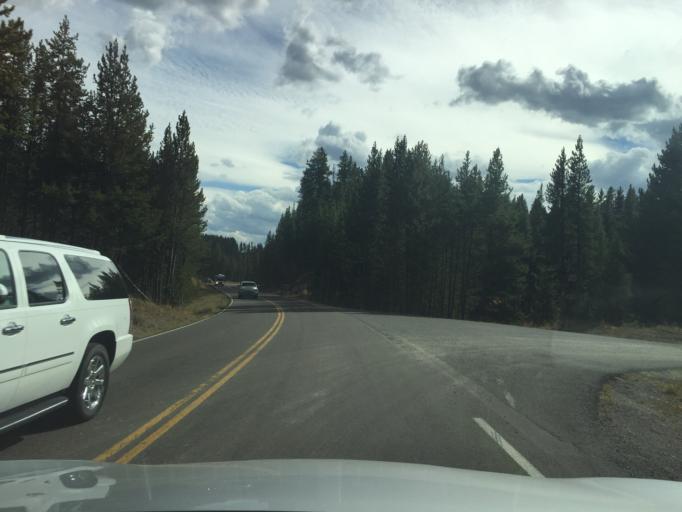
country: US
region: Montana
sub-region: Gallatin County
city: West Yellowstone
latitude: 44.7101
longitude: -110.5053
